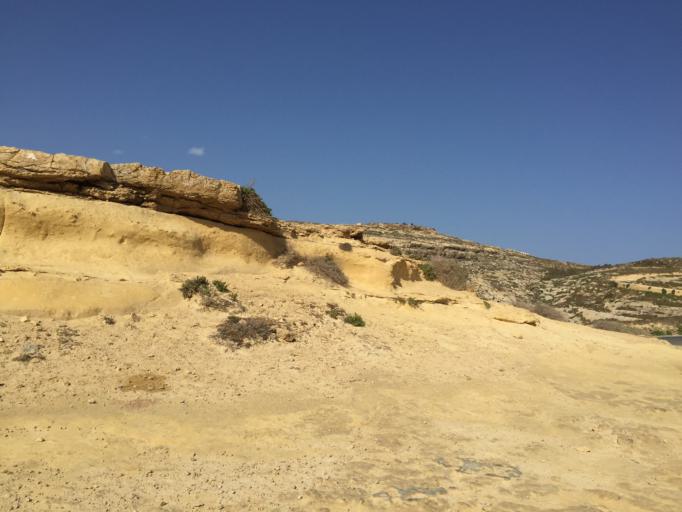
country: MT
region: Saint Lawrence
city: San Lawrenz
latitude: 36.0515
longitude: 14.1902
